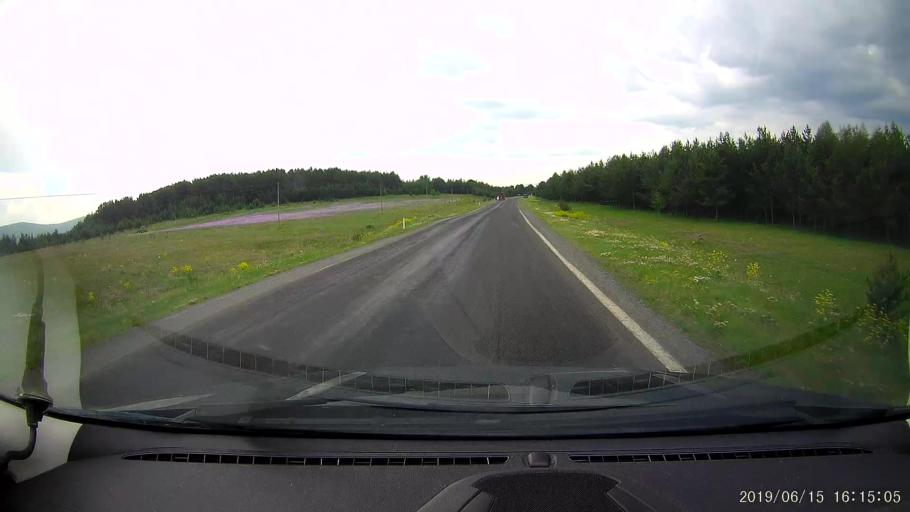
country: TR
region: Ardahan
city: Hanak
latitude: 41.2723
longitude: 42.8530
